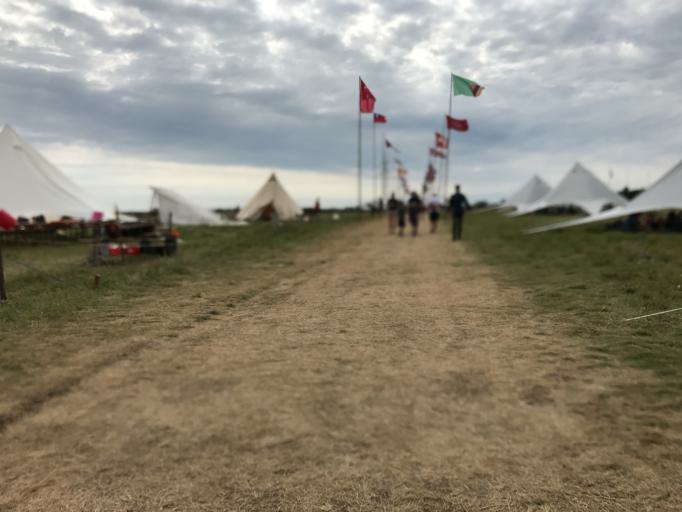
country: SE
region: Skane
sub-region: Kristianstads Kommun
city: Fjalkinge
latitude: 56.0033
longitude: 14.2978
